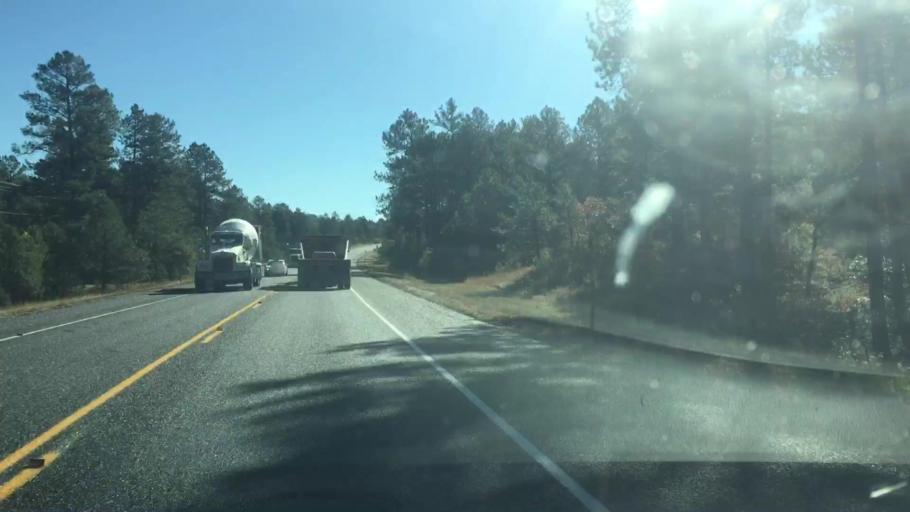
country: US
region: Colorado
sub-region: Elbert County
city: Ponderosa Park
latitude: 39.3781
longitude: -104.7015
